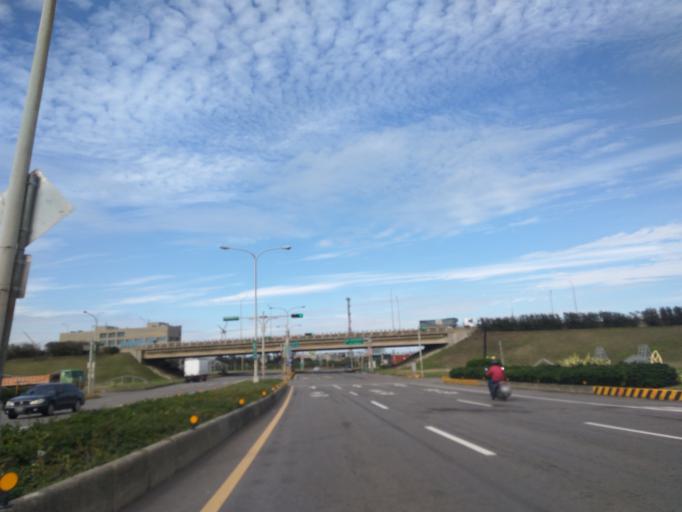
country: TW
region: Taiwan
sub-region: Hsinchu
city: Zhubei
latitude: 25.0289
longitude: 121.0547
